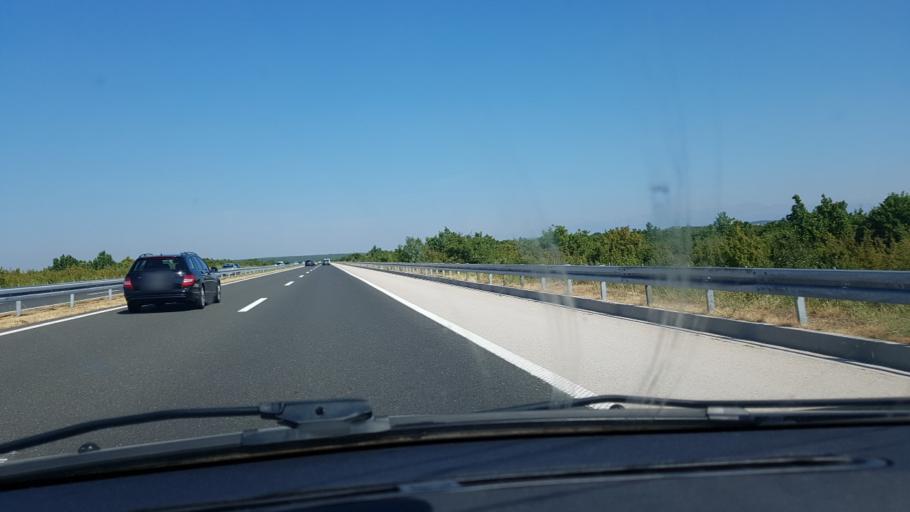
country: HR
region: Zadarska
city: Benkovac
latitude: 43.9786
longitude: 15.6392
